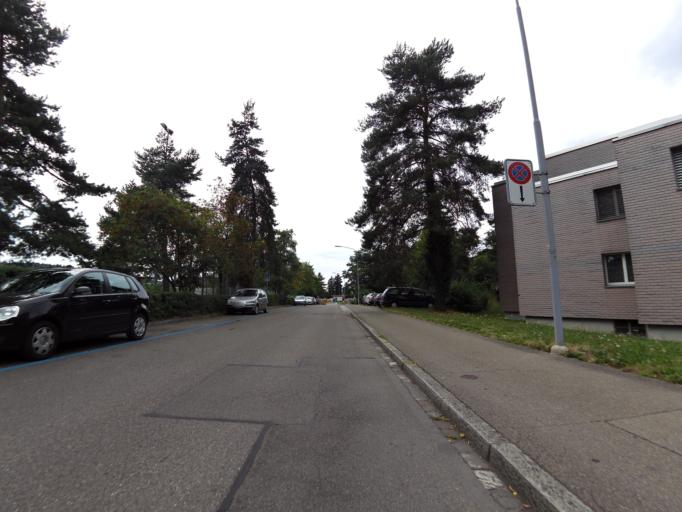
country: CH
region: Zurich
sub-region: Bezirk Zuerich
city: Zuerich (Kreis 11) / Affoltern
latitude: 47.4213
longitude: 8.5117
